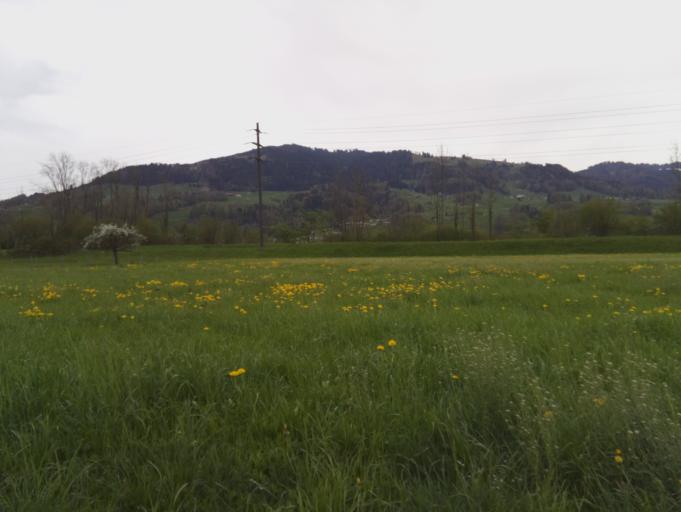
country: CH
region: Schwyz
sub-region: Bezirk March
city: Lachen
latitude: 47.1837
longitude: 8.8828
